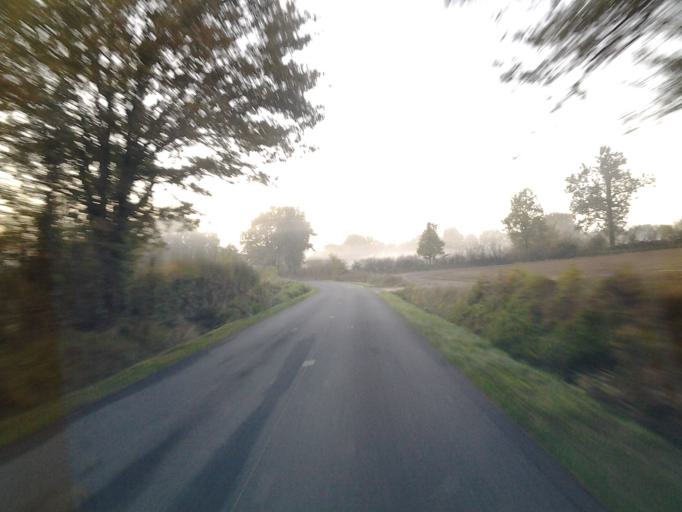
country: FR
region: Pays de la Loire
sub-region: Departement de la Vendee
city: Chateau-Guibert
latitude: 46.6312
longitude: -1.2330
